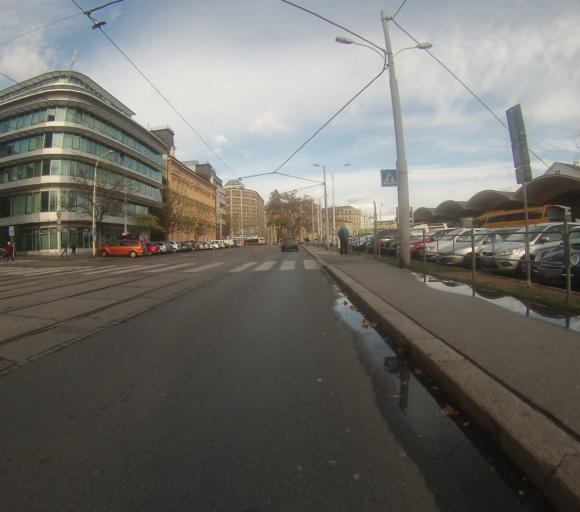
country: CZ
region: South Moravian
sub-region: Mesto Brno
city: Brno
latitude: 49.1934
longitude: 16.6139
